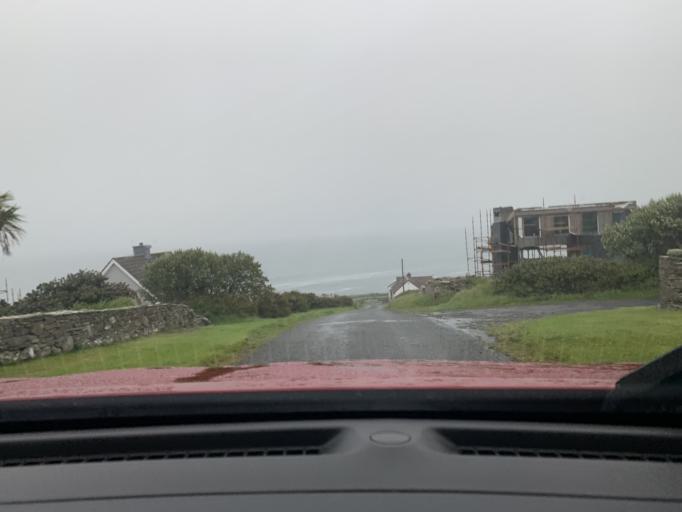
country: IE
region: Ulster
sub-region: County Donegal
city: Killybegs
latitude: 54.4698
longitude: -8.4550
